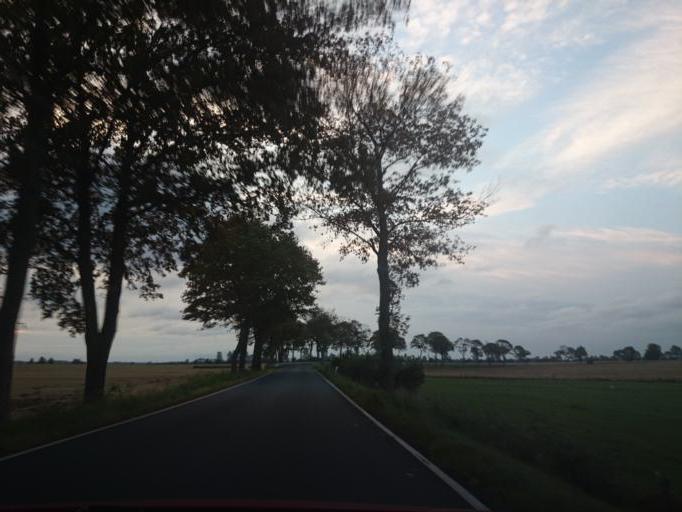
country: DE
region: Mecklenburg-Vorpommern
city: Barth
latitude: 54.3413
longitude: 12.7870
